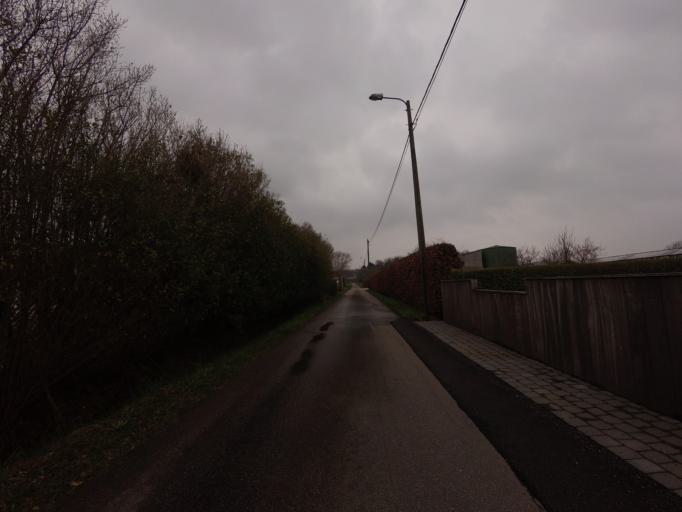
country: BE
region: Flanders
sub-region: Provincie Antwerpen
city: Sint-Katelijne-Waver
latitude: 51.0696
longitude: 4.5813
